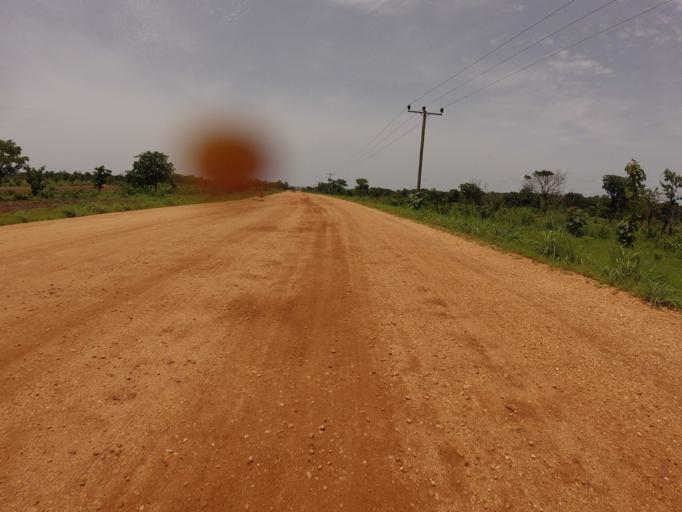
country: GH
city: Kpandae
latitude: 8.7219
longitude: 0.1278
